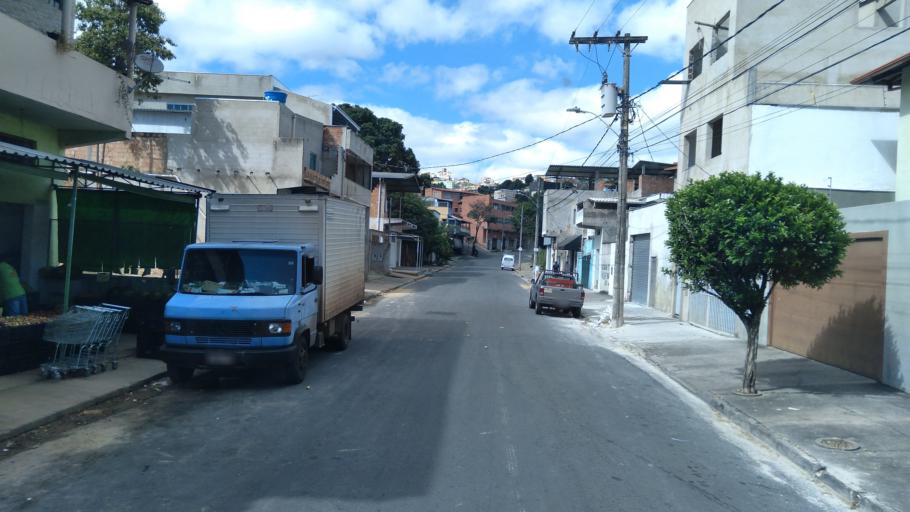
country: BR
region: Minas Gerais
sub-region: Belo Horizonte
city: Belo Horizonte
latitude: -19.8627
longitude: -43.9104
